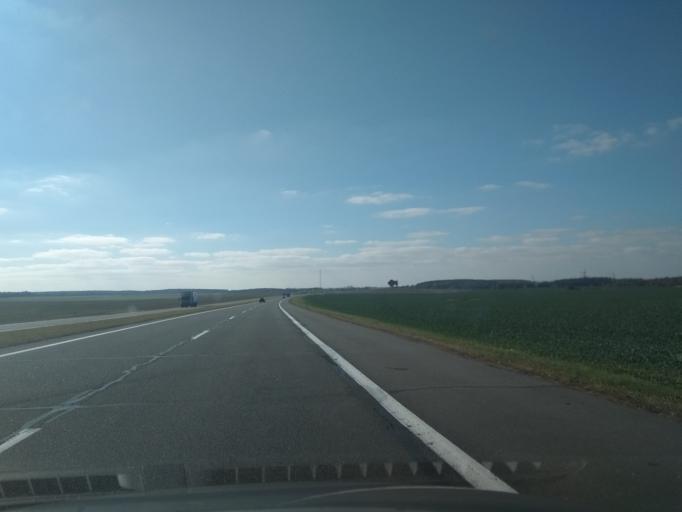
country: BY
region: Minsk
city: Snow
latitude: 53.3060
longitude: 26.3850
